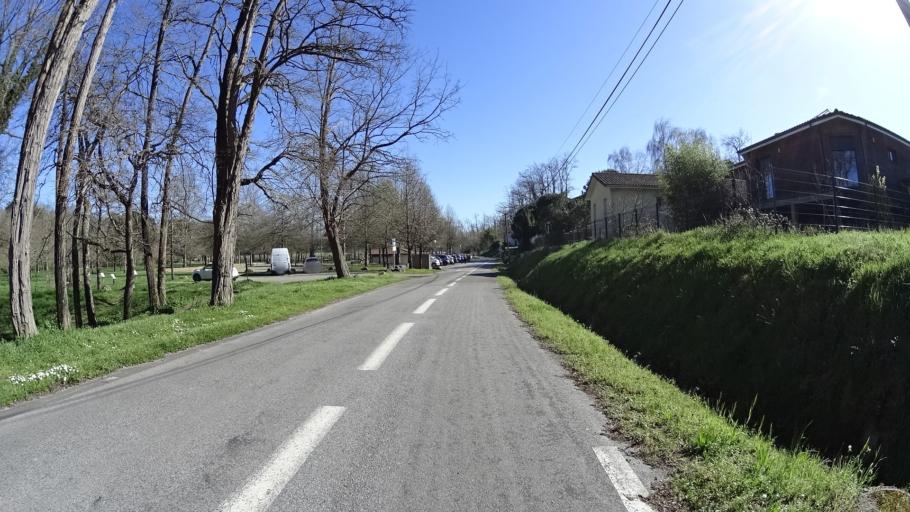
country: FR
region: Aquitaine
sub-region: Departement des Landes
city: Saint-Paul-les-Dax
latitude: 43.7330
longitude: -1.0734
